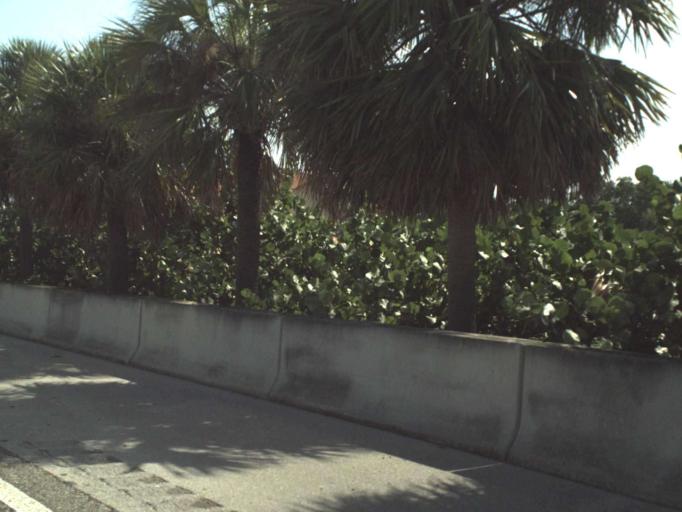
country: US
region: Florida
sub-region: Palm Beach County
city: North Palm Beach
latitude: 26.8099
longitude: -80.0980
